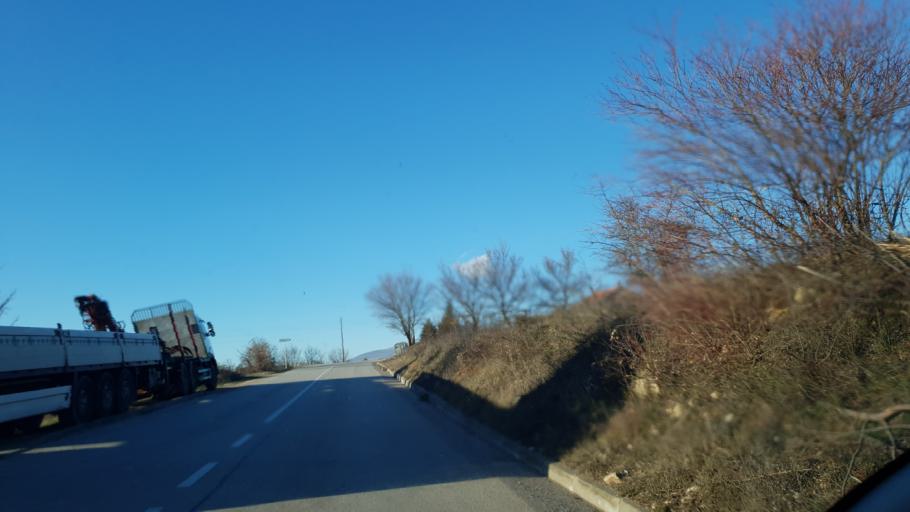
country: HR
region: Splitsko-Dalmatinska
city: Gala
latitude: 43.7369
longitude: 16.6830
